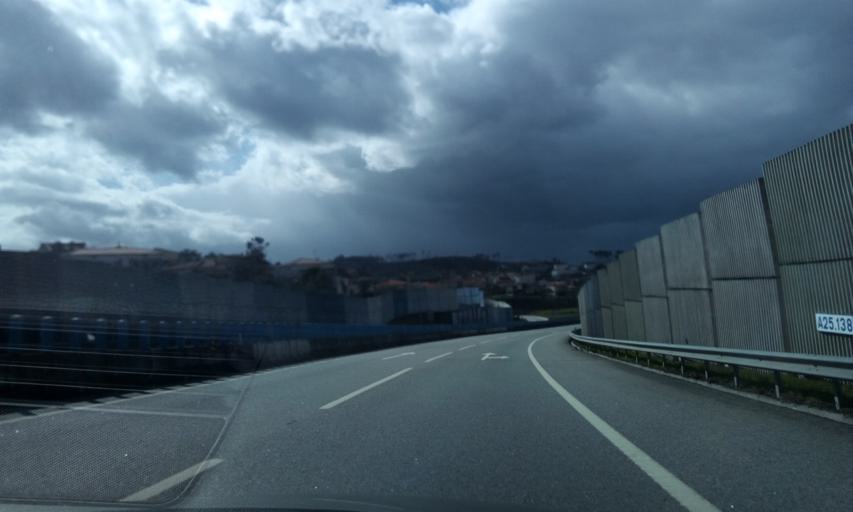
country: PT
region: Viseu
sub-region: Mangualde
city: Mangualde
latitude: 40.6273
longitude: -7.7976
